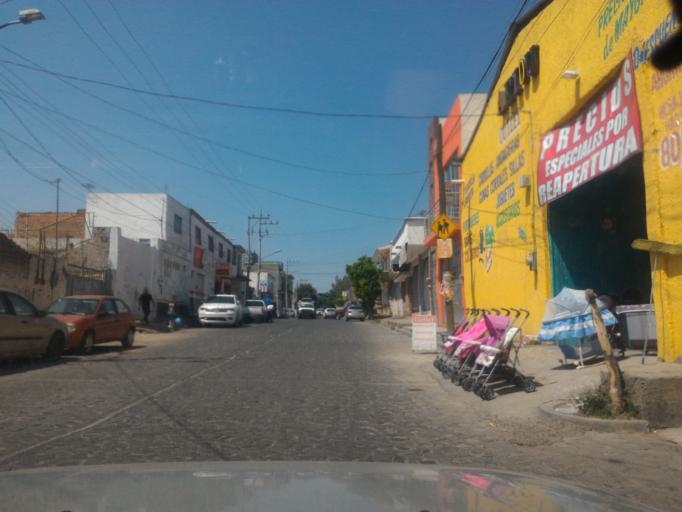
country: MX
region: Jalisco
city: Santa Anita
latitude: 20.5537
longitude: -103.4464
